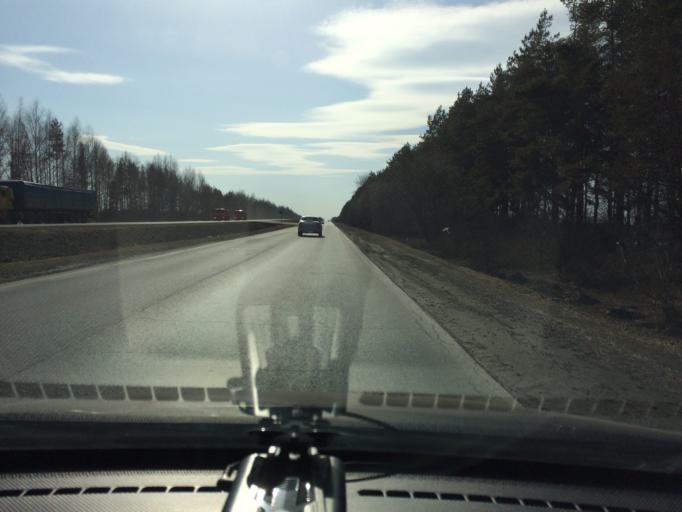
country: RU
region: Mariy-El
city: Yoshkar-Ola
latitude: 56.7269
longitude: 48.1308
